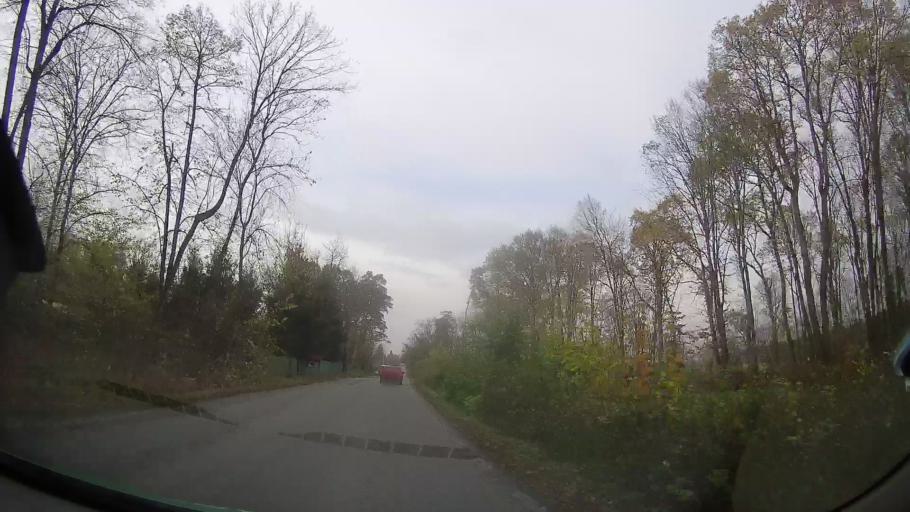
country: RO
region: Prahova
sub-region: Comuna Gorgota
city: Potigrafu
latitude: 44.7700
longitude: 26.1101
